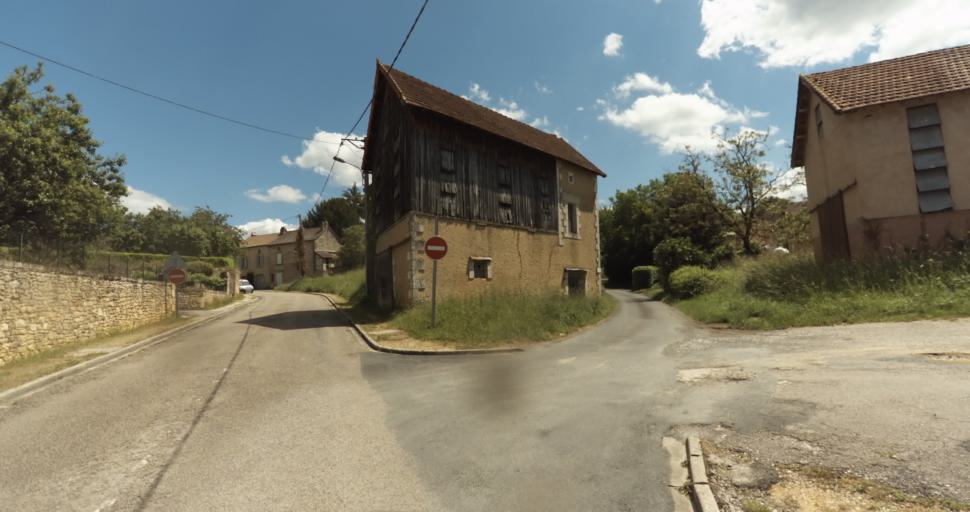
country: FR
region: Aquitaine
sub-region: Departement de la Dordogne
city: Belves
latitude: 44.8214
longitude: 0.9839
